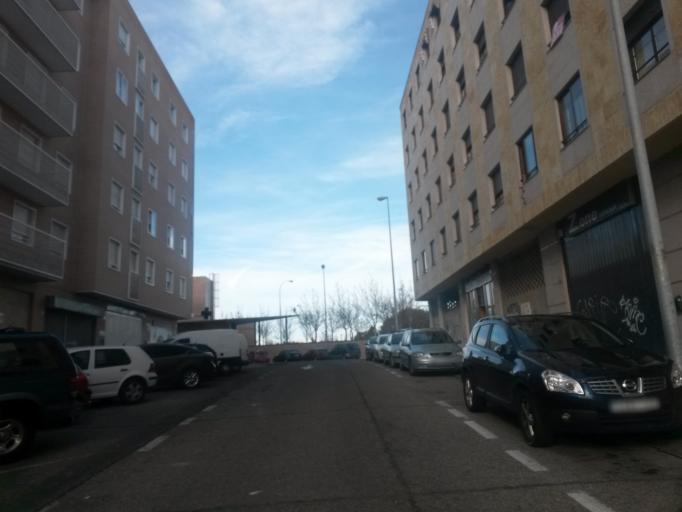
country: ES
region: Castille and Leon
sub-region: Provincia de Salamanca
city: Salamanca
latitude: 40.9790
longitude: -5.6546
